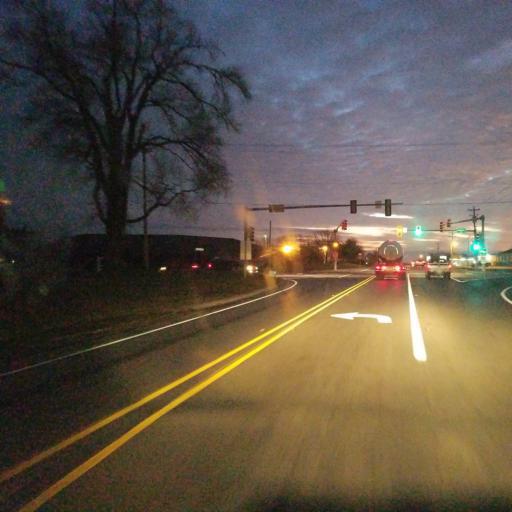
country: US
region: Illinois
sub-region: Peoria County
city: Bellevue
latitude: 40.6886
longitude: -89.6944
